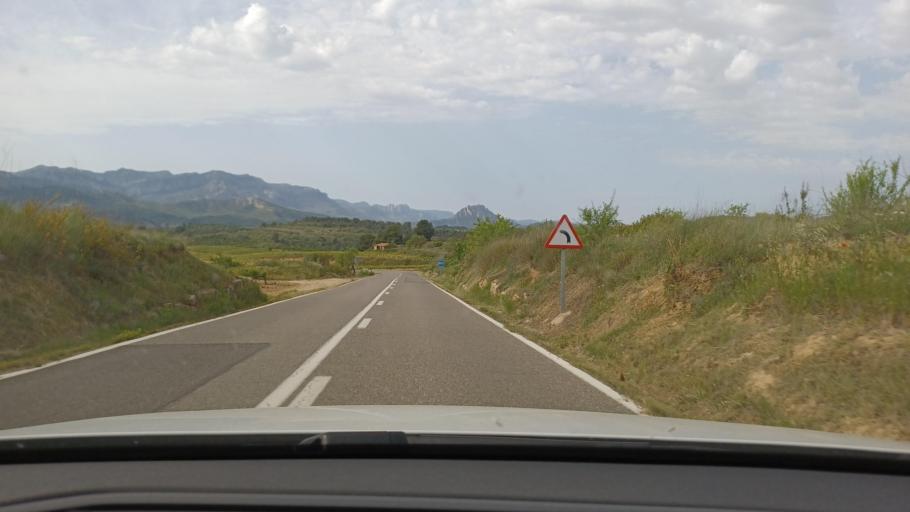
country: ES
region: Catalonia
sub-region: Provincia de Tarragona
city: Bot
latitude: 41.0282
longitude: 0.3803
